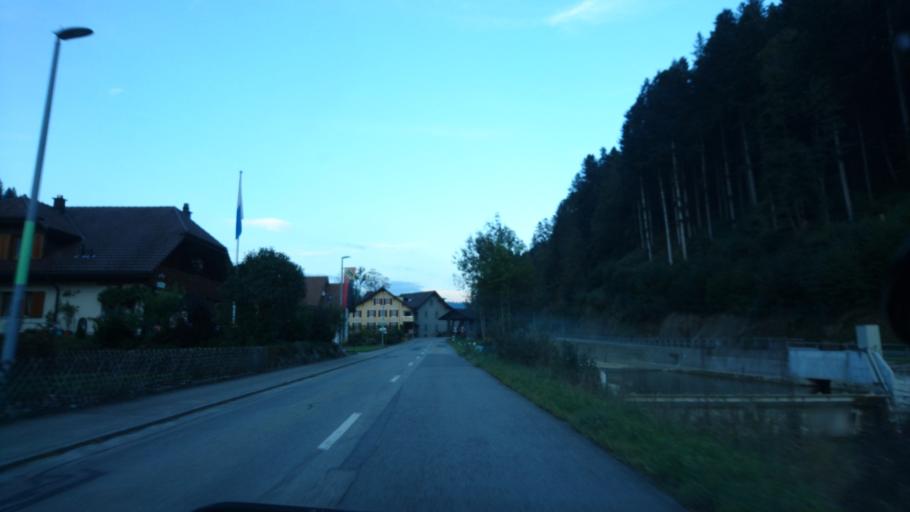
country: CH
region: Bern
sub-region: Emmental District
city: Trubschachen
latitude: 46.9254
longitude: 7.8488
